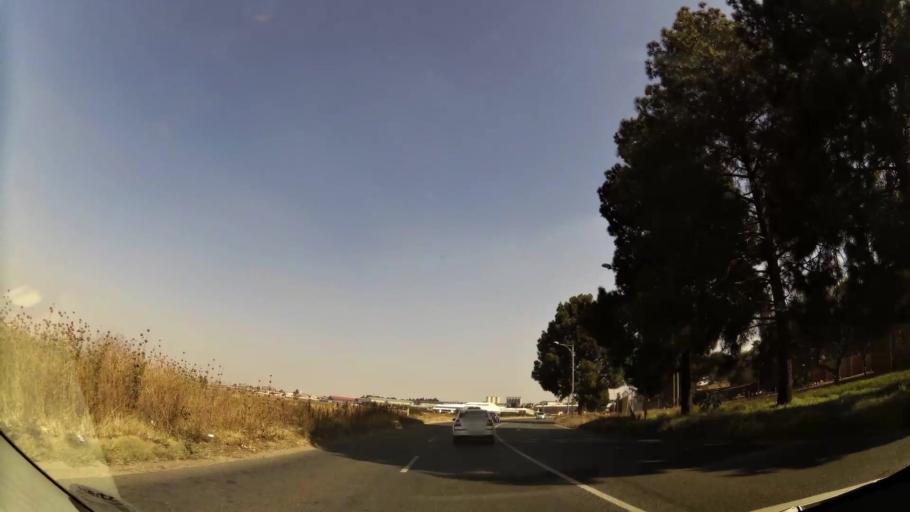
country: ZA
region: Gauteng
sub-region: City of Johannesburg Metropolitan Municipality
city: Roodepoort
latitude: -26.1548
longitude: 27.8081
